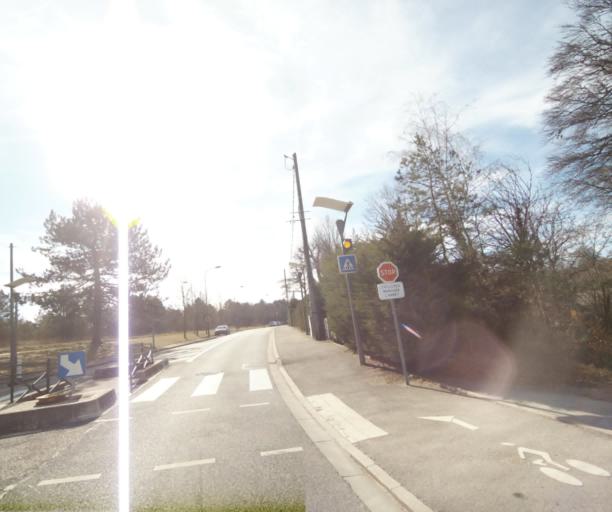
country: FR
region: Lorraine
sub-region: Departement de Meurthe-et-Moselle
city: Villers-les-Nancy
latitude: 48.6653
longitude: 6.1367
